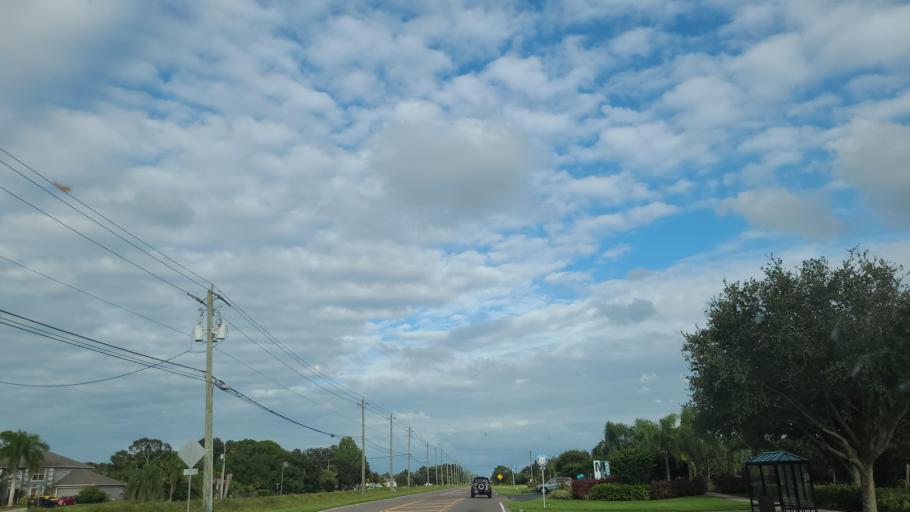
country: US
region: Florida
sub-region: Brevard County
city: June Park
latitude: 27.9990
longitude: -80.6869
